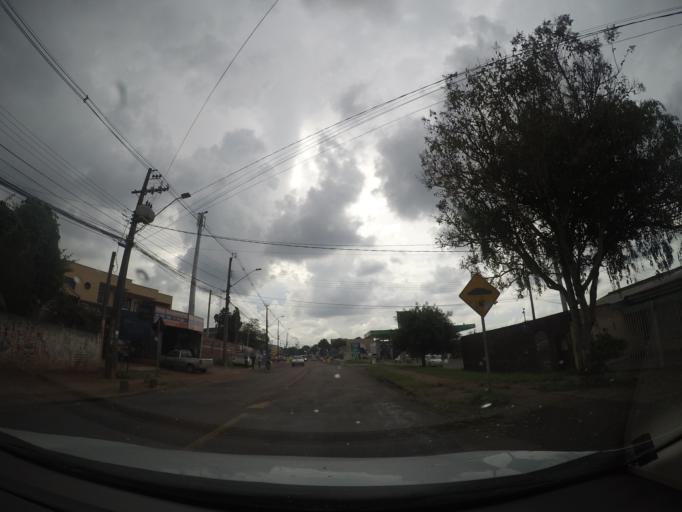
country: BR
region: Parana
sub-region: Sao Jose Dos Pinhais
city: Sao Jose dos Pinhais
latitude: -25.5384
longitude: -49.2418
